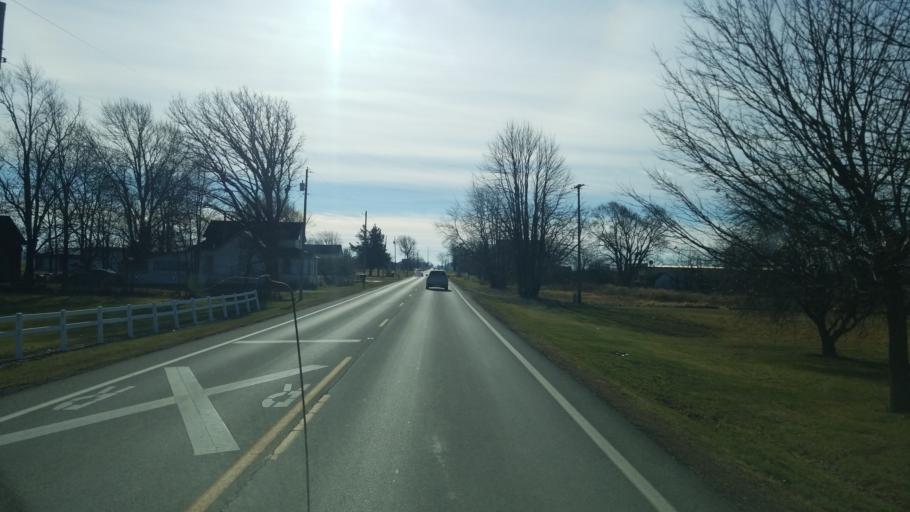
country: US
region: Ohio
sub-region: Putnam County
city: Leipsic
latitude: 41.0936
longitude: -83.9863
